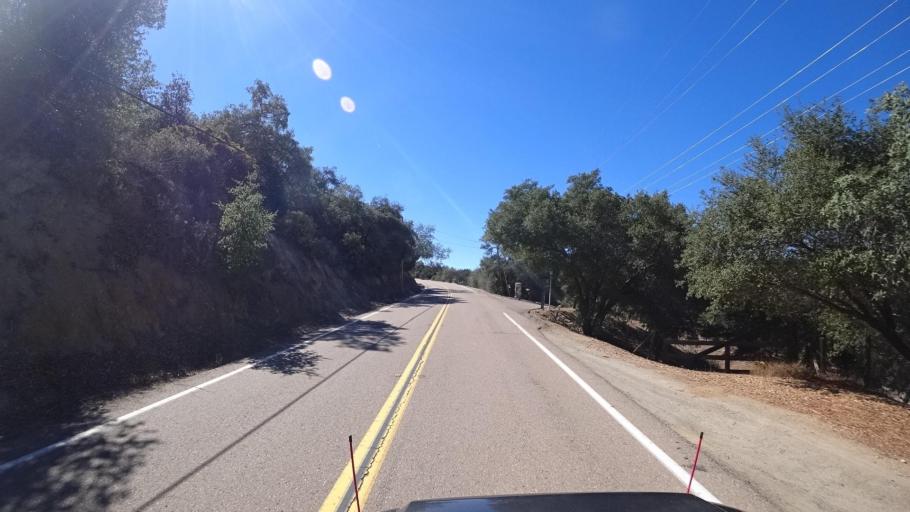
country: US
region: California
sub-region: San Diego County
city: Descanso
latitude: 32.7846
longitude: -116.6649
